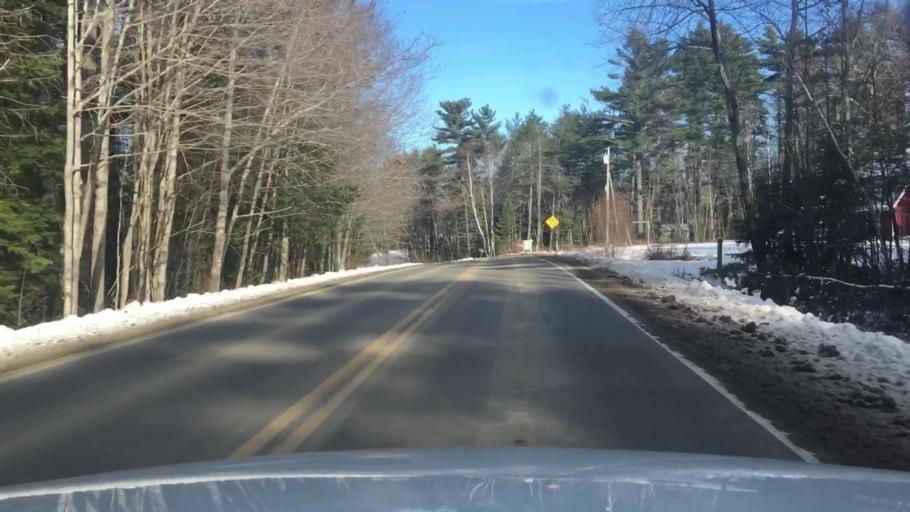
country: US
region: Maine
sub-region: Lincoln County
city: Wiscasset
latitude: 43.9708
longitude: -69.6699
